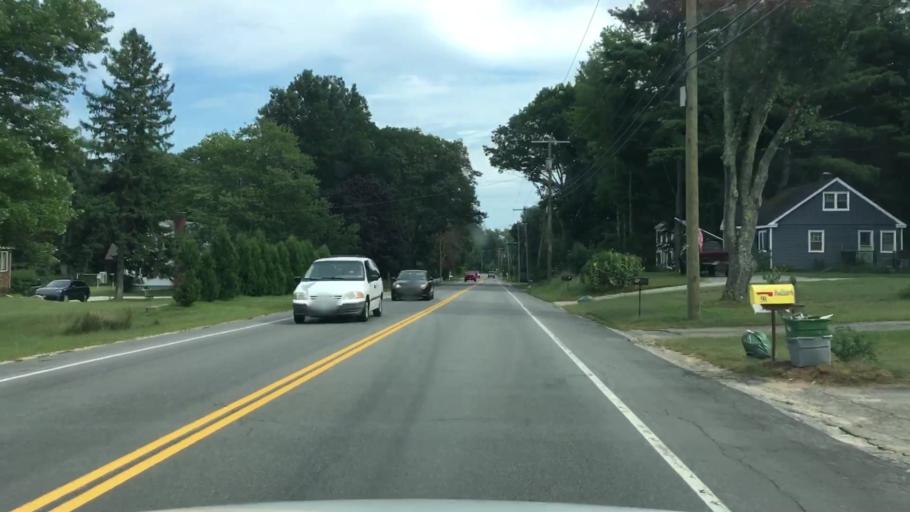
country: US
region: New Hampshire
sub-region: Strafford County
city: Madbury
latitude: 43.1910
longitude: -70.9251
